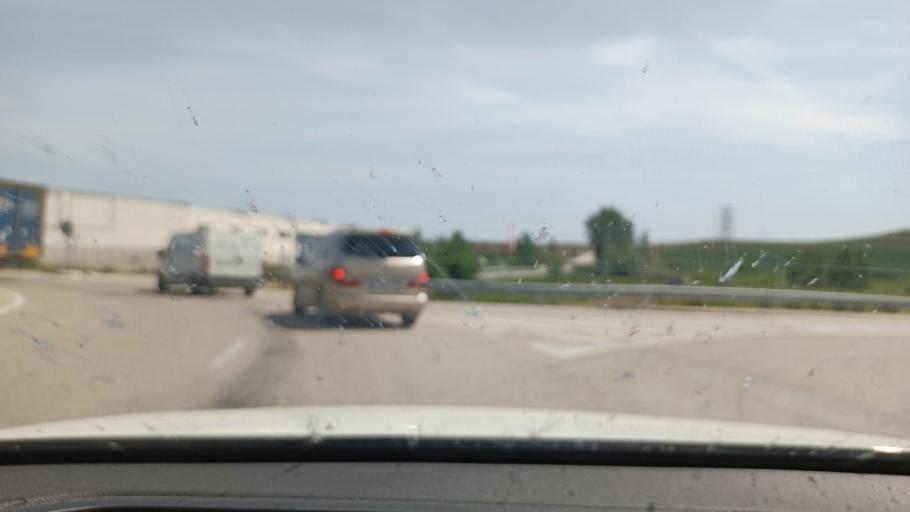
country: ES
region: Castille and Leon
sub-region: Provincia de Soria
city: Almazan
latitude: 41.4708
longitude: -2.5401
